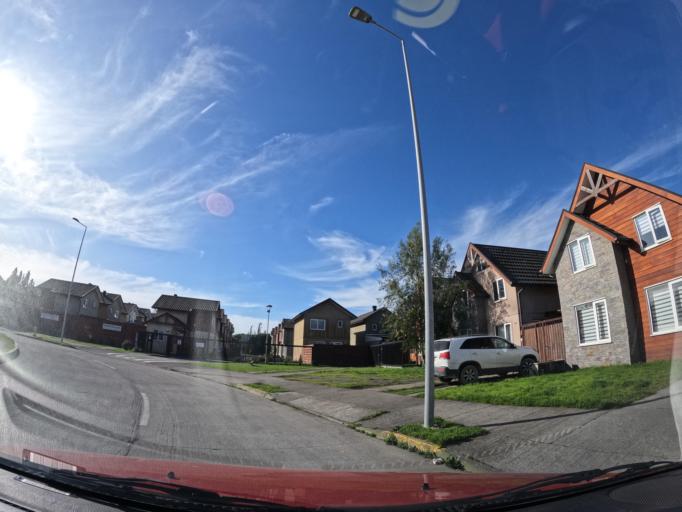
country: CL
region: Biobio
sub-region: Provincia de Concepcion
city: Concepcion
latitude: -36.7693
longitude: -73.0675
